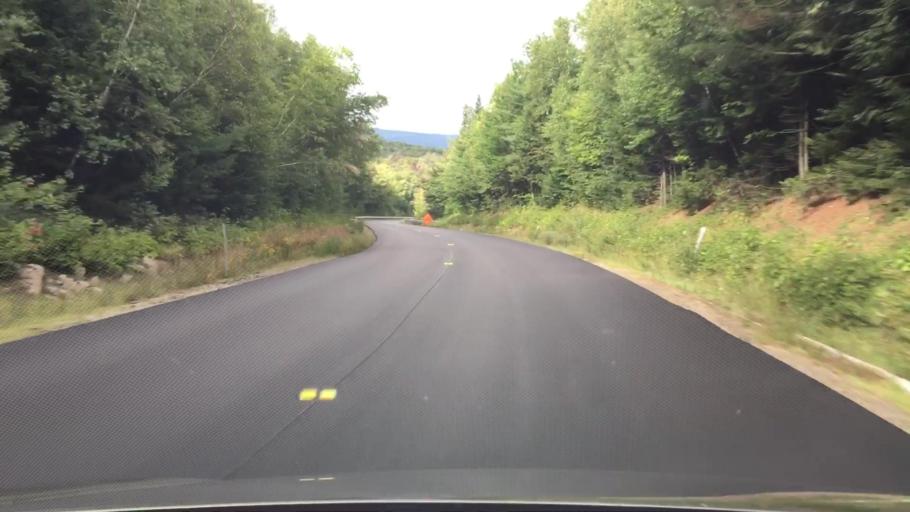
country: US
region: New Hampshire
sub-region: Carroll County
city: Sandwich
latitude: 44.0182
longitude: -71.4509
